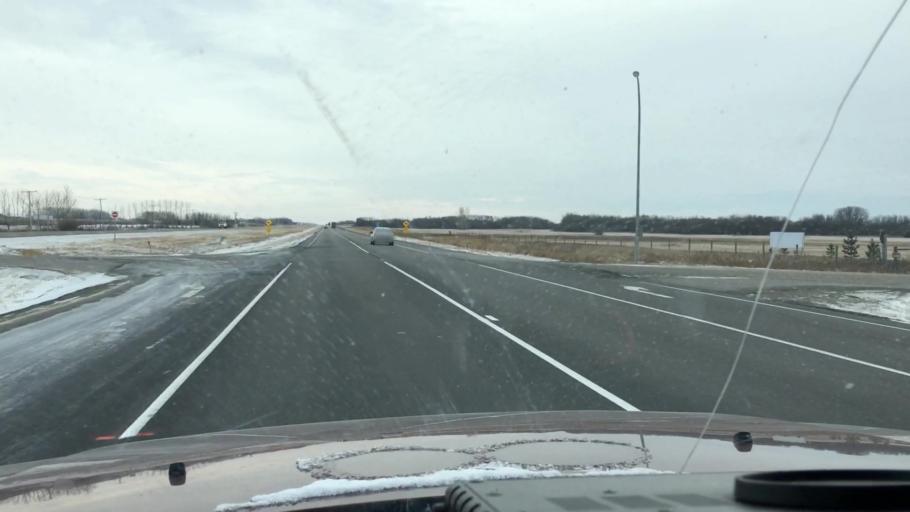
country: CA
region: Saskatchewan
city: Saskatoon
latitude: 51.9983
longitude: -106.5672
